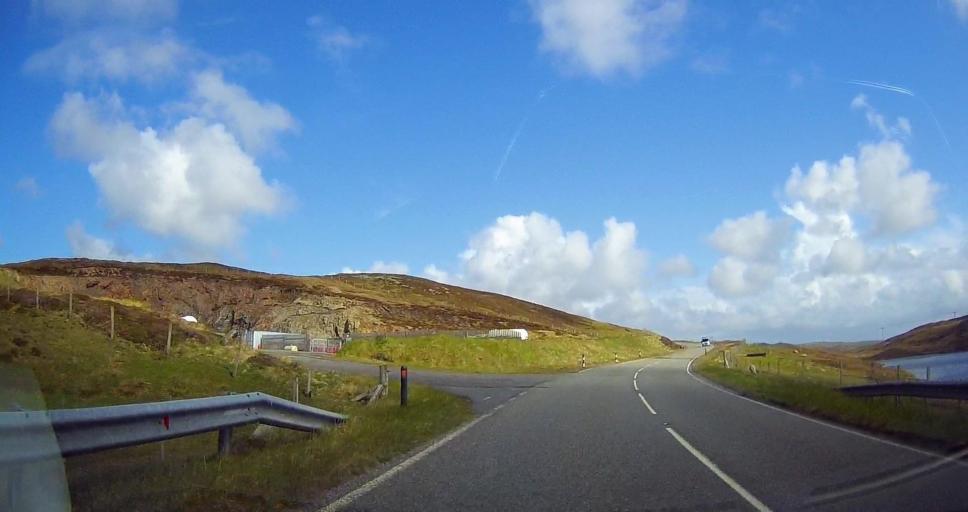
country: GB
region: Scotland
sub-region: Shetland Islands
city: Lerwick
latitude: 60.4460
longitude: -1.3964
